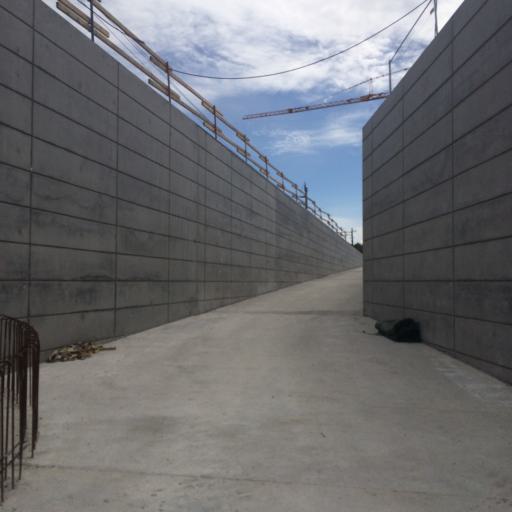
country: SE
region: Stockholm
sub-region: Jarfalla Kommun
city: Jakobsberg
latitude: 59.4030
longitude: 17.8695
